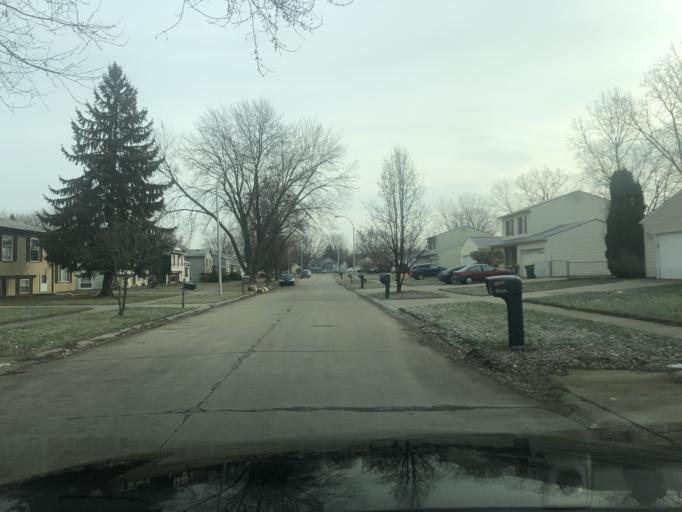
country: US
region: Michigan
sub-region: Wayne County
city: Taylor
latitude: 42.1871
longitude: -83.3195
